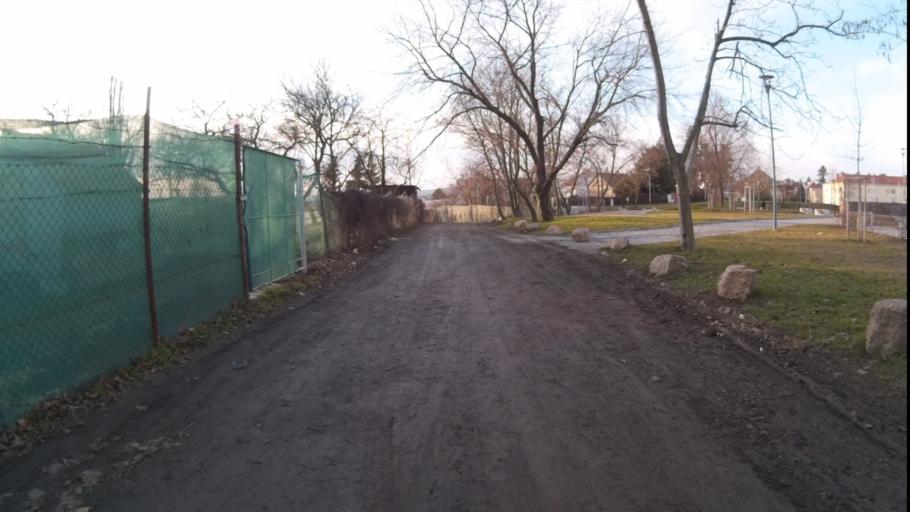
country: CZ
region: South Moravian
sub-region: Mesto Brno
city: Brno
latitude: 49.1936
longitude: 16.5863
